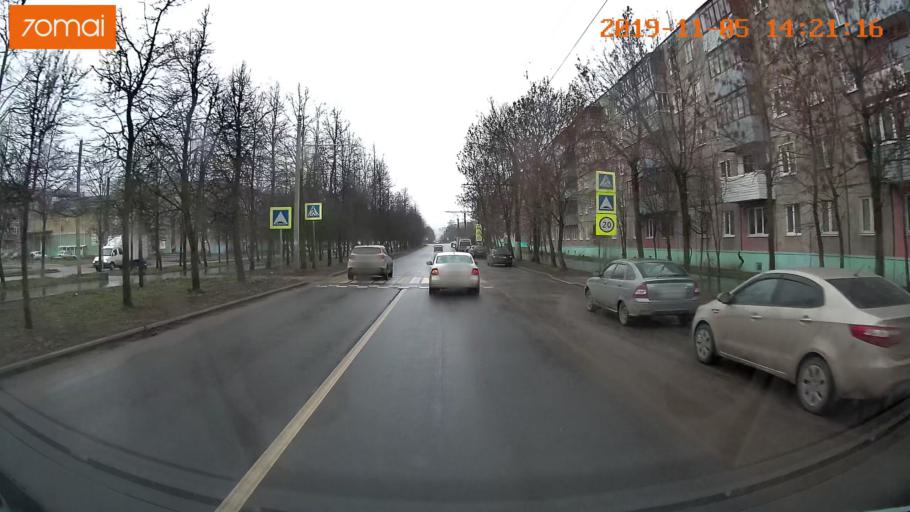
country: RU
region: Ivanovo
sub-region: Gorod Ivanovo
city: Ivanovo
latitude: 56.9583
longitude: 41.0121
